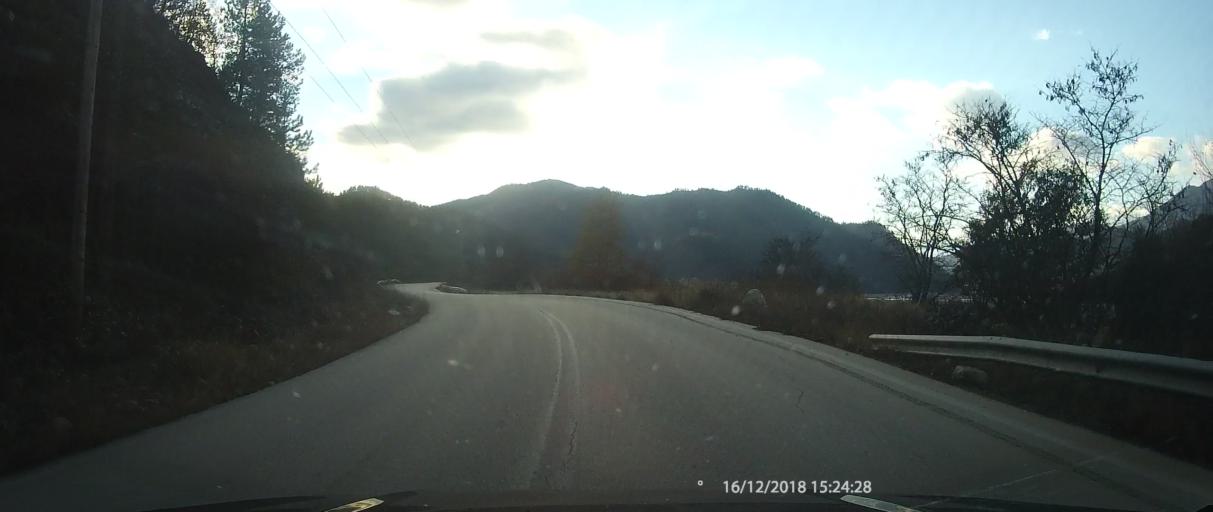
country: GR
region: Epirus
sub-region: Nomos Ioanninon
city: Konitsa
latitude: 40.1382
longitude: 20.7912
